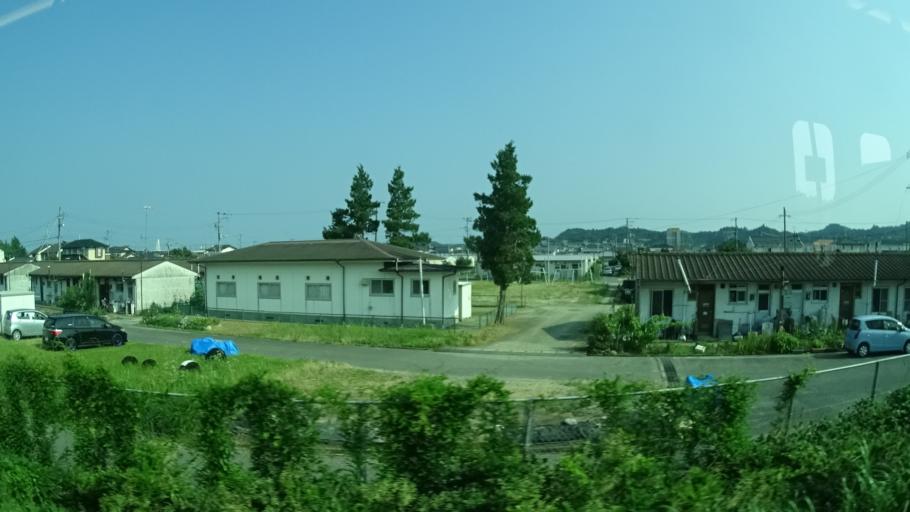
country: JP
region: Fukushima
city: Iwaki
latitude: 37.0668
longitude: 140.9356
